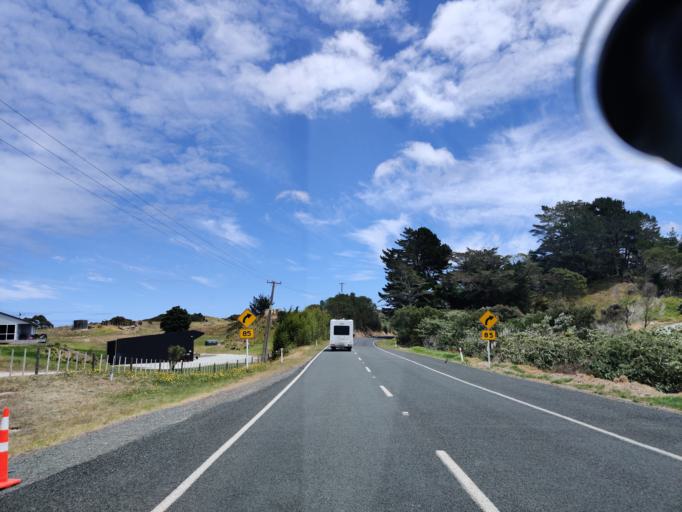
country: NZ
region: Northland
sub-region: Far North District
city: Kaitaia
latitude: -34.7689
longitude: 173.0791
